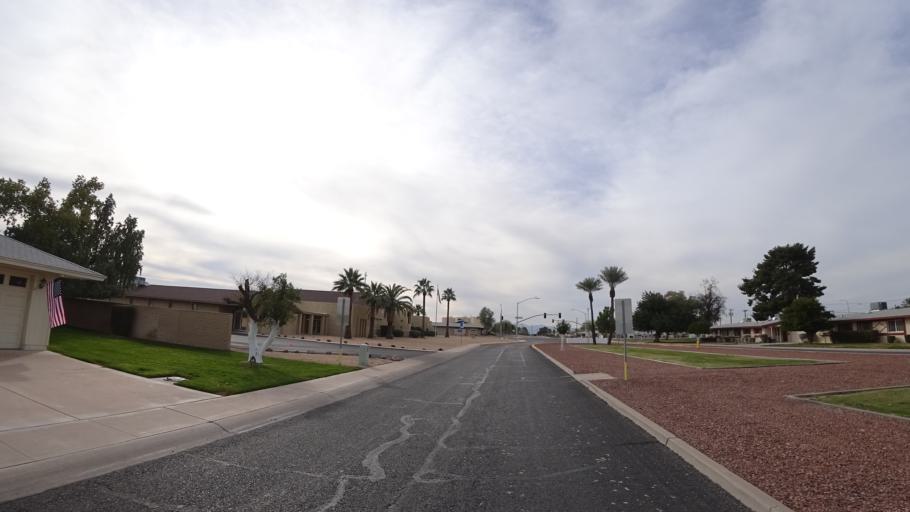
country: US
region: Arizona
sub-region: Maricopa County
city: Youngtown
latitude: 33.5799
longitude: -112.2976
